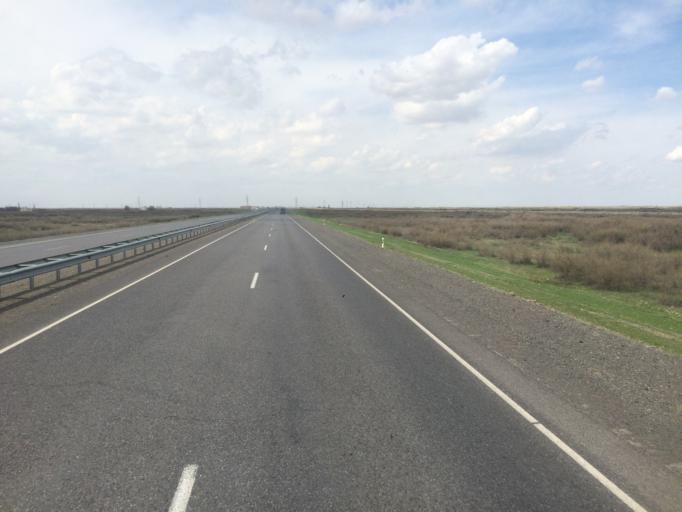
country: KZ
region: Qyzylorda
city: Zhangaqorghan
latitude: 43.9960
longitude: 67.2256
